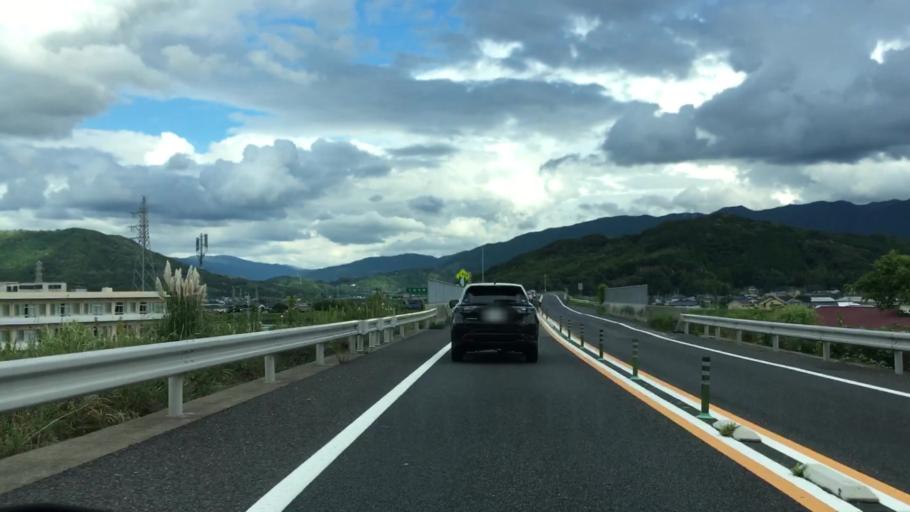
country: JP
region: Saga Prefecture
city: Karatsu
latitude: 33.4120
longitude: 129.9832
